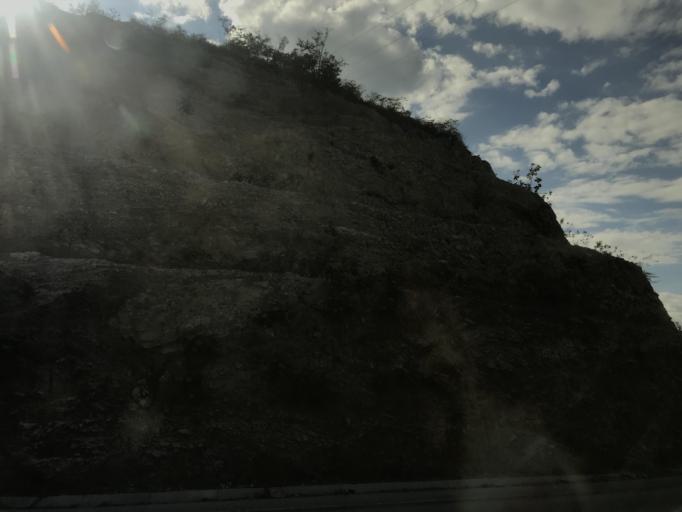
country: GT
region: El Progreso
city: Guastatoya
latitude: 14.8475
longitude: -90.1139
